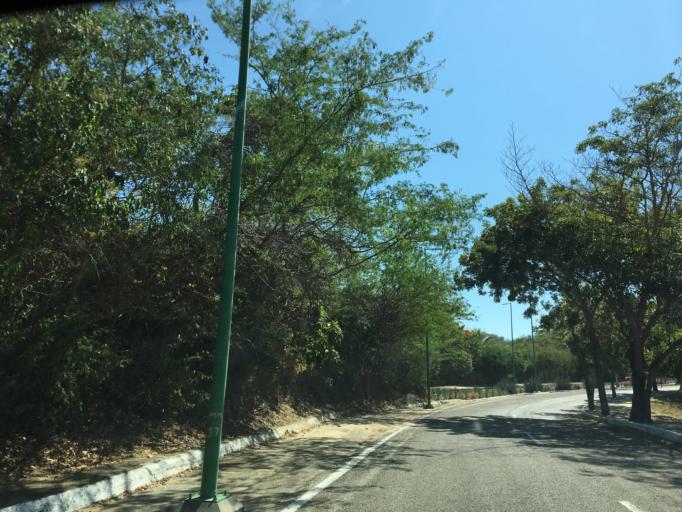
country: MX
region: Oaxaca
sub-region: Santa Maria Huatulco
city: Crucecita
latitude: 15.7774
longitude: -96.0781
